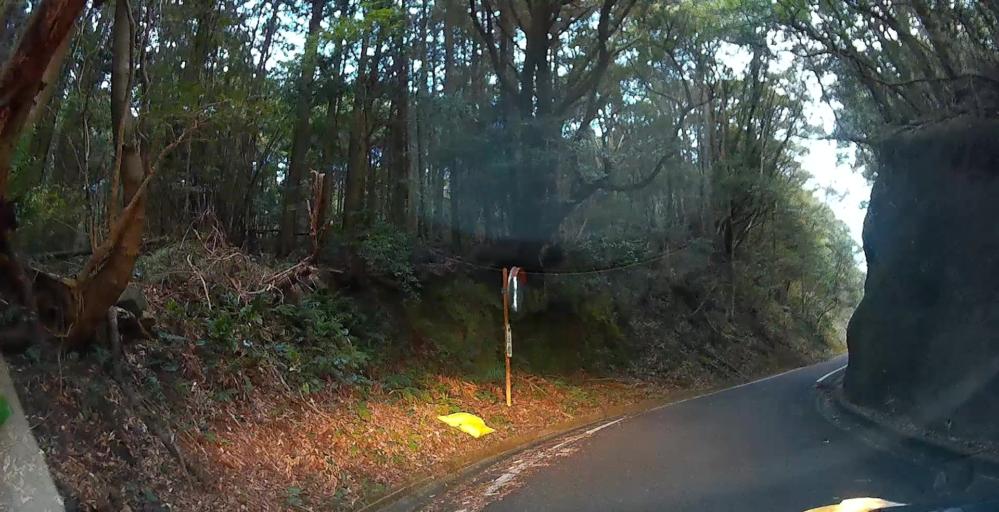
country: JP
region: Kagoshima
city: Izumi
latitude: 32.1180
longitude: 130.4162
